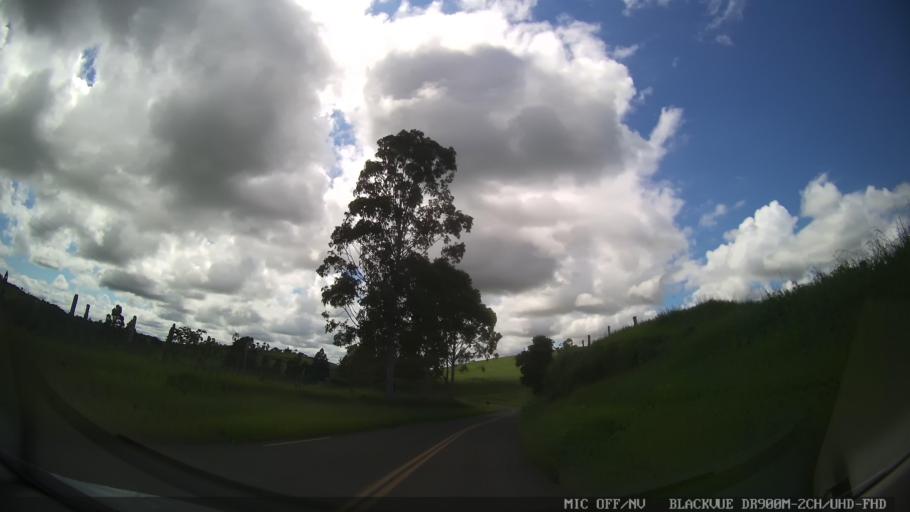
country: BR
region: Sao Paulo
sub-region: Braganca Paulista
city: Braganca Paulista
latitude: -22.8627
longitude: -46.6466
